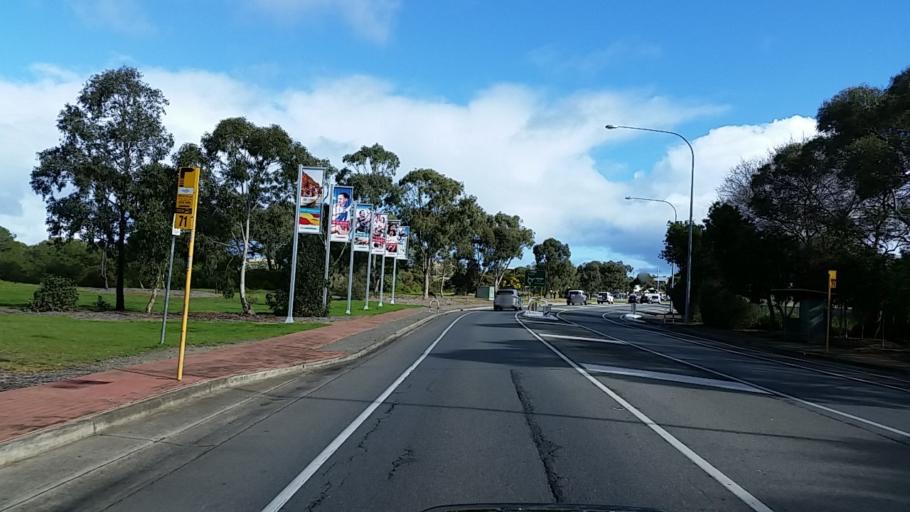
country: AU
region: South Australia
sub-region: Adelaide
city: Port Noarlunga
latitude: -35.1479
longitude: 138.4754
